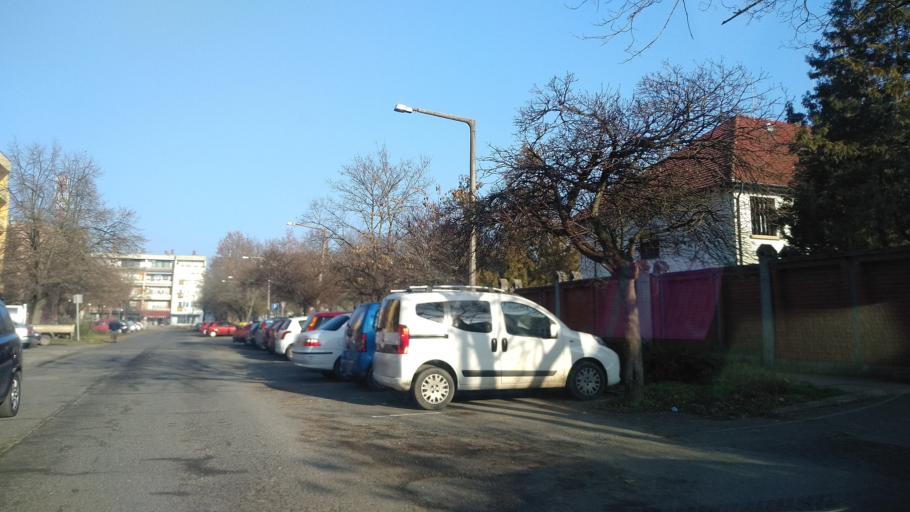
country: HU
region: Somogy
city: Barcs
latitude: 45.9597
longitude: 17.4625
